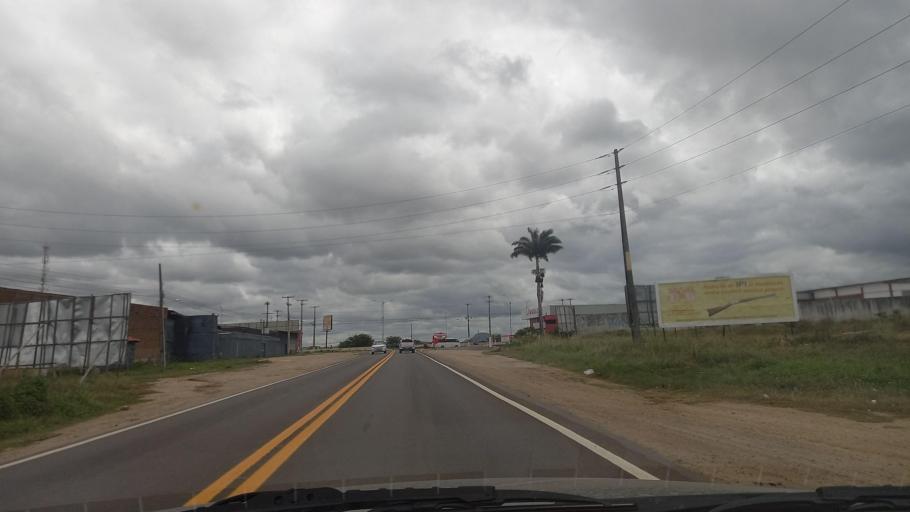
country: BR
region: Pernambuco
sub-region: Caruaru
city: Caruaru
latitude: -8.2529
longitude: -35.9734
